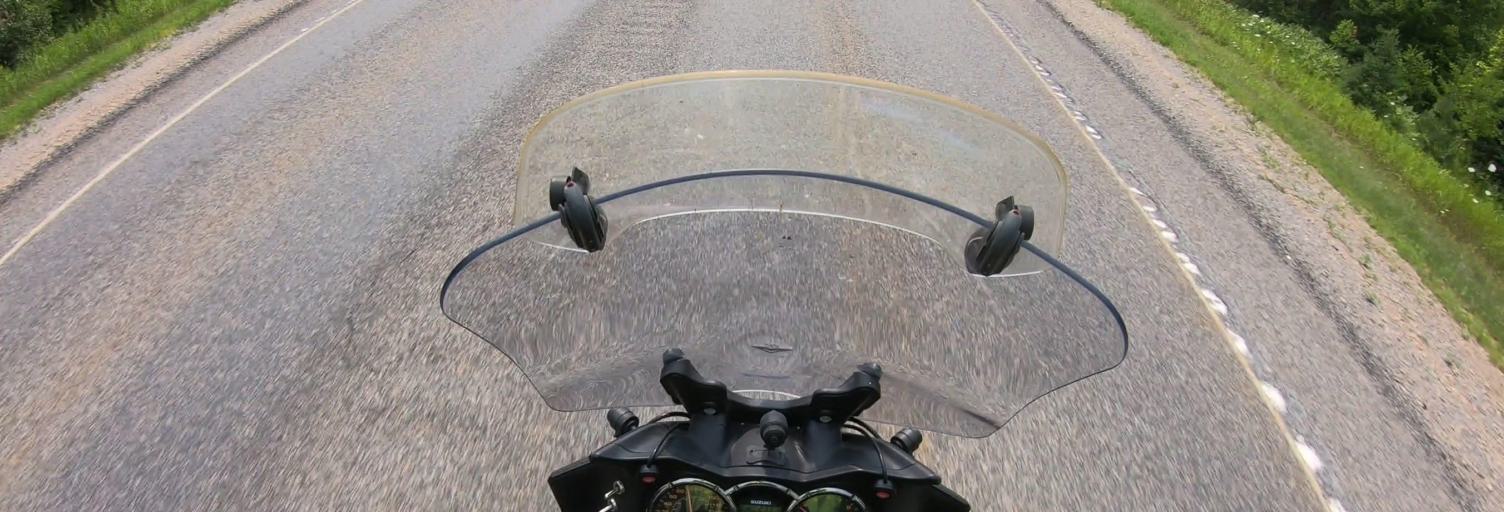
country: US
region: Michigan
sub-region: Alger County
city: Munising
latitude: 46.3623
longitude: -86.7131
